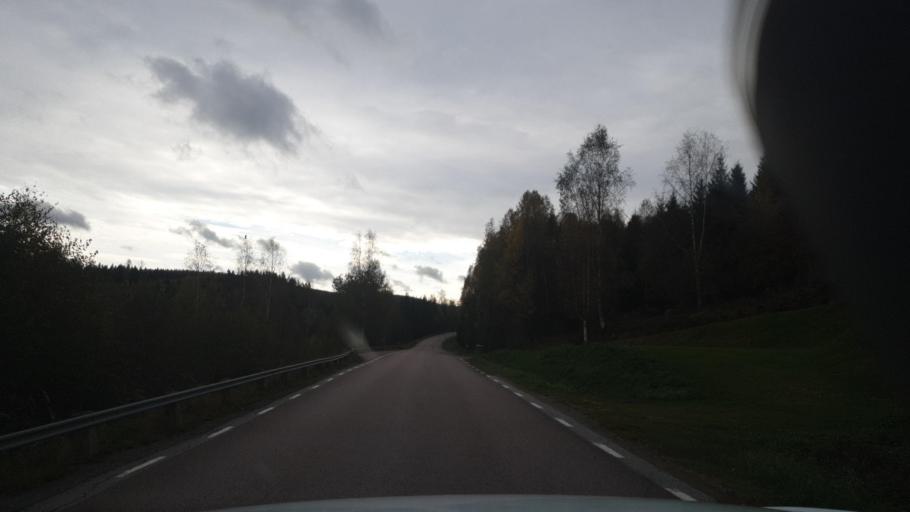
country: SE
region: Vaermland
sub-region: Arvika Kommun
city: Arvika
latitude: 59.7291
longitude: 12.7981
